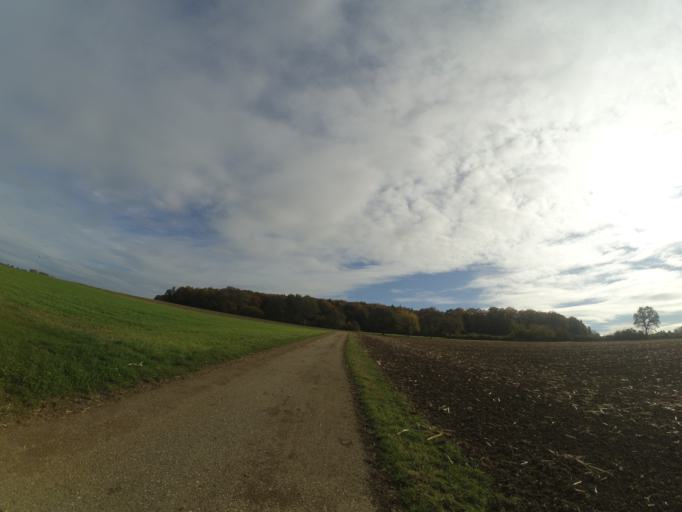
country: DE
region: Baden-Wuerttemberg
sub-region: Tuebingen Region
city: Lonsee
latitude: 48.5529
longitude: 9.9257
